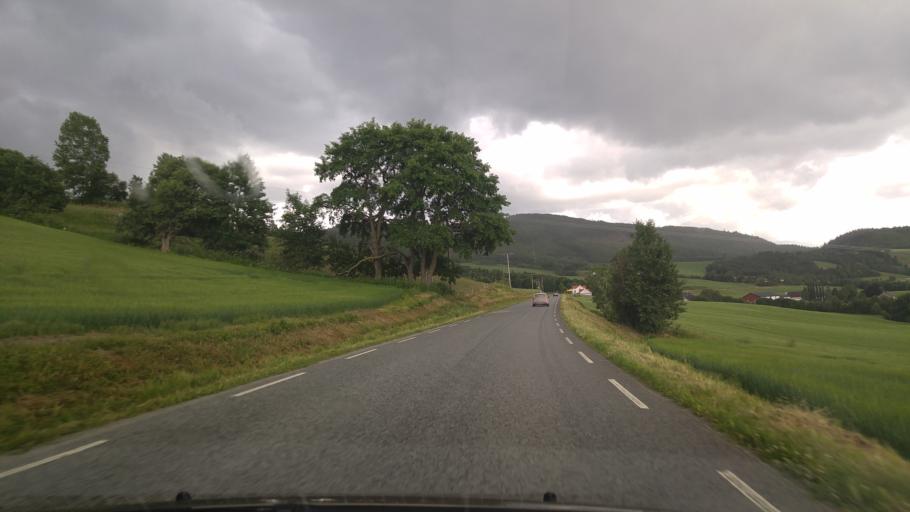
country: NO
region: Nord-Trondelag
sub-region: Levanger
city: Skogn
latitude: 63.6860
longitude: 11.2340
